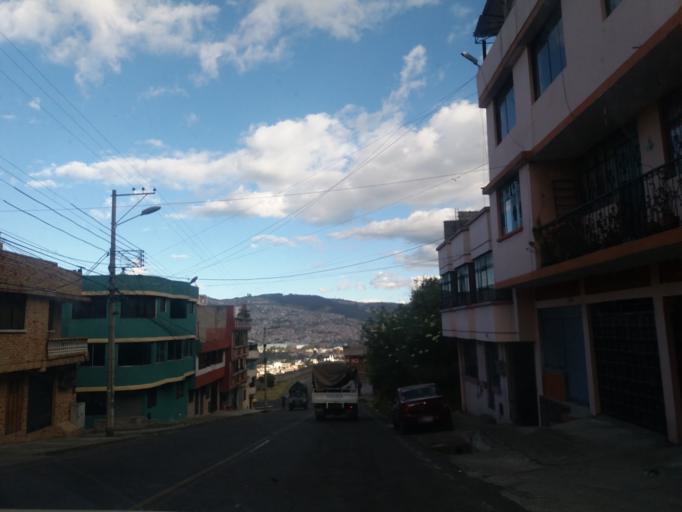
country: EC
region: Pichincha
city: Quito
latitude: -0.2322
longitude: -78.5328
